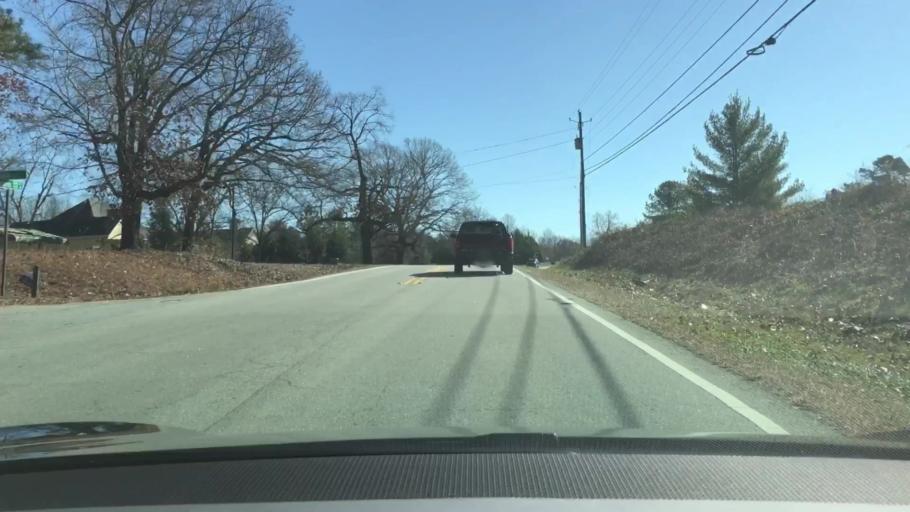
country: US
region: Georgia
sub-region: Gwinnett County
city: Dacula
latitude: 33.9579
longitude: -83.8667
